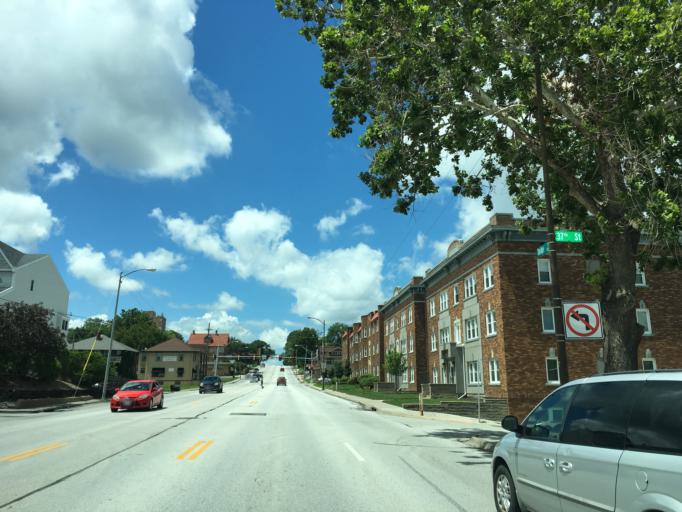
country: US
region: Nebraska
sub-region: Douglas County
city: Omaha
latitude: 41.2596
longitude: -95.9672
